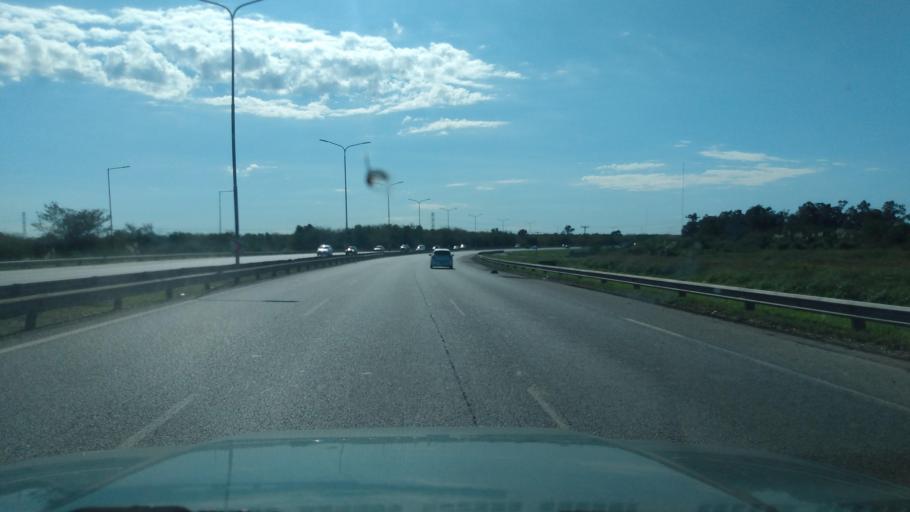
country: AR
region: Buenos Aires
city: Hurlingham
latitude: -34.5568
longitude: -58.6274
